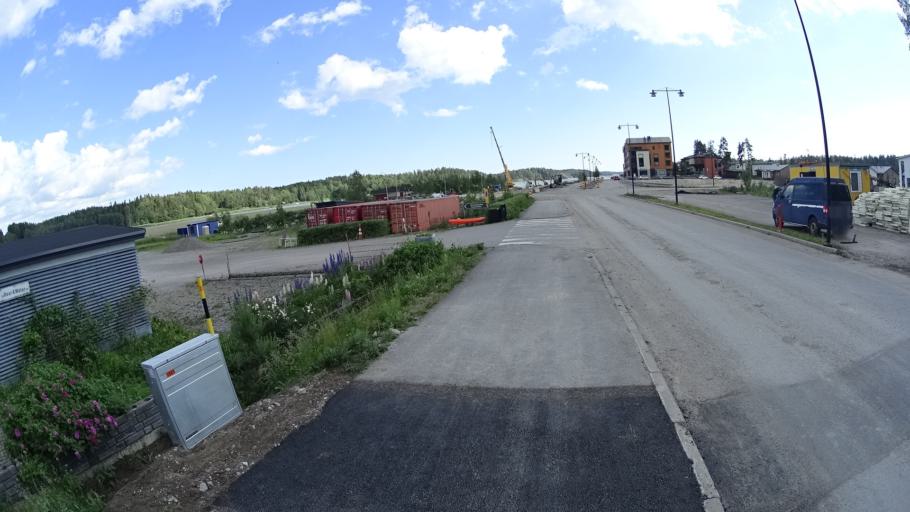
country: FI
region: Uusimaa
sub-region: Helsinki
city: Sibbo
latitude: 60.2610
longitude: 25.2350
